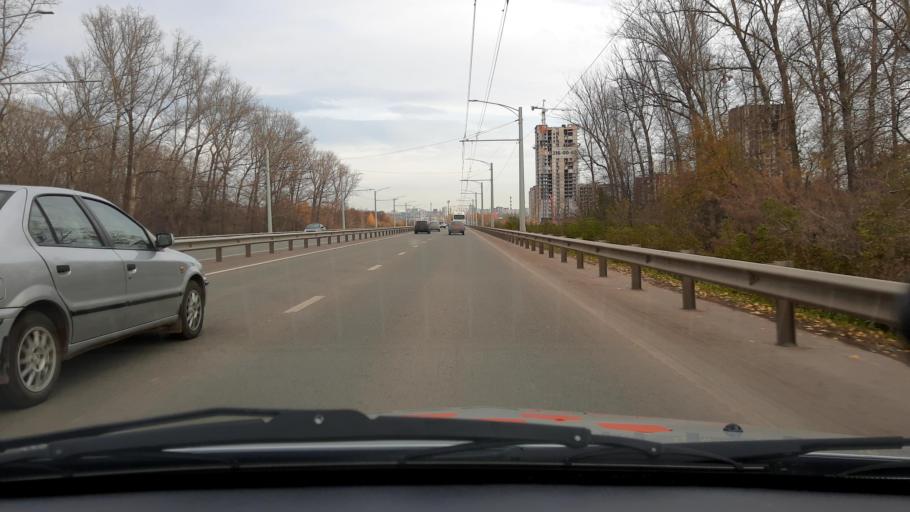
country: RU
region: Bashkortostan
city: Mikhaylovka
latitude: 54.7746
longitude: 55.8954
